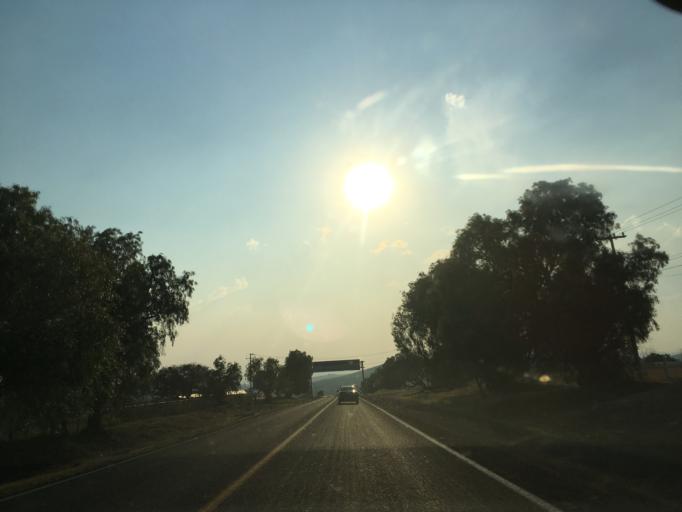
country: MX
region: Michoacan
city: Charo
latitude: 19.7468
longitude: -101.0562
